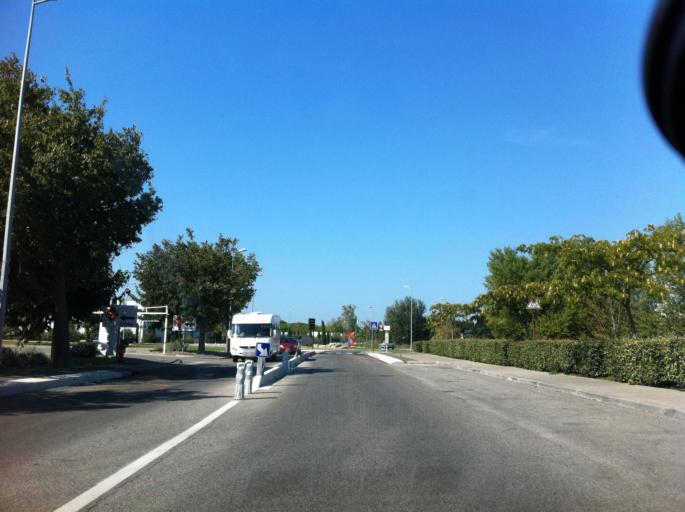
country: FR
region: Provence-Alpes-Cote d'Azur
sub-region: Departement du Vaucluse
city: Montfavet
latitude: 43.9248
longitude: 4.8596
